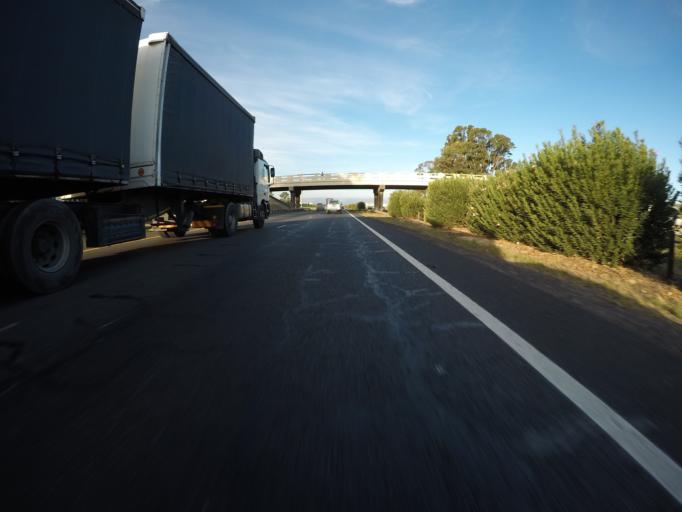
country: ZA
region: Western Cape
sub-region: City of Cape Town
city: Kraaifontein
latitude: -33.8356
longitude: 18.7350
